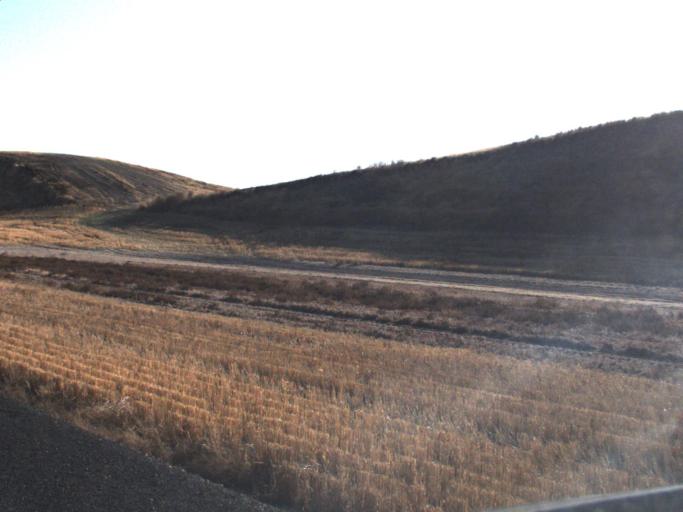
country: US
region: Washington
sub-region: Adams County
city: Ritzville
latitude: 46.8390
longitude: -118.3321
